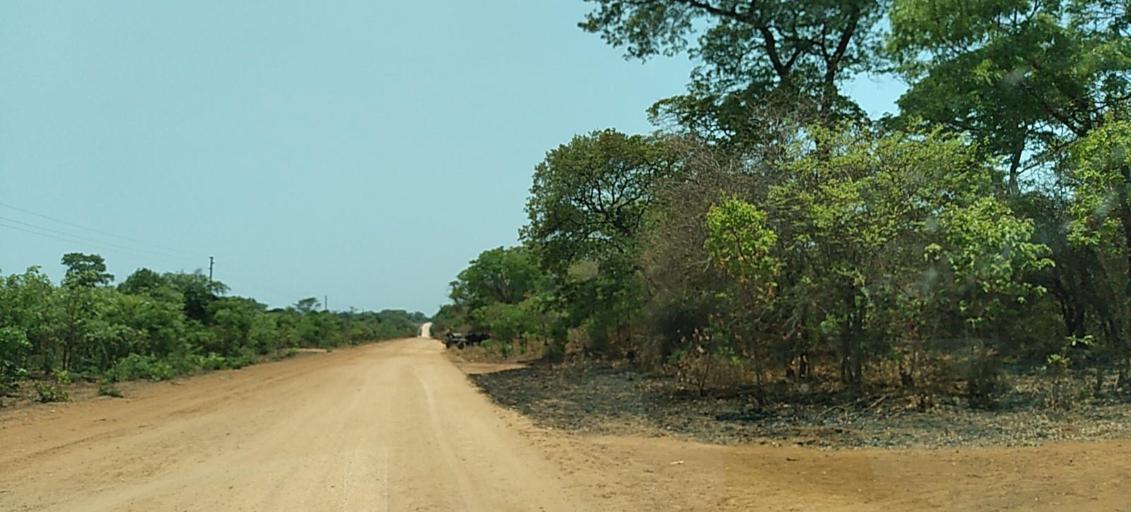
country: ZM
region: Copperbelt
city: Mpongwe
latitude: -13.8183
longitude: 27.8444
